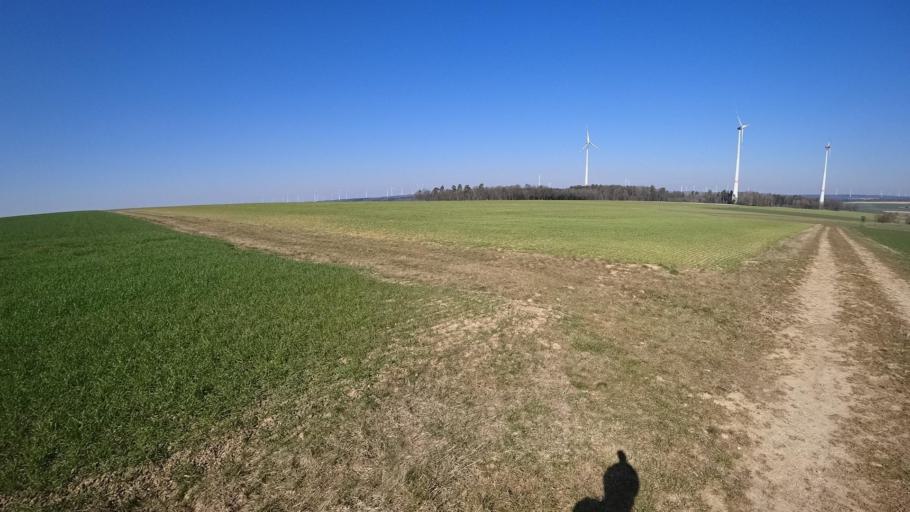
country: DE
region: Rheinland-Pfalz
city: Mutterschied
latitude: 49.9975
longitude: 7.5780
